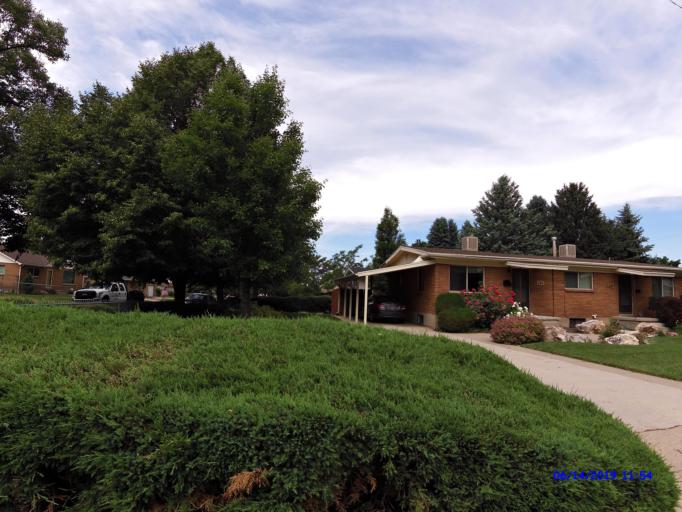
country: US
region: Utah
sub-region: Weber County
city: Ogden
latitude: 41.2569
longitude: -111.9450
